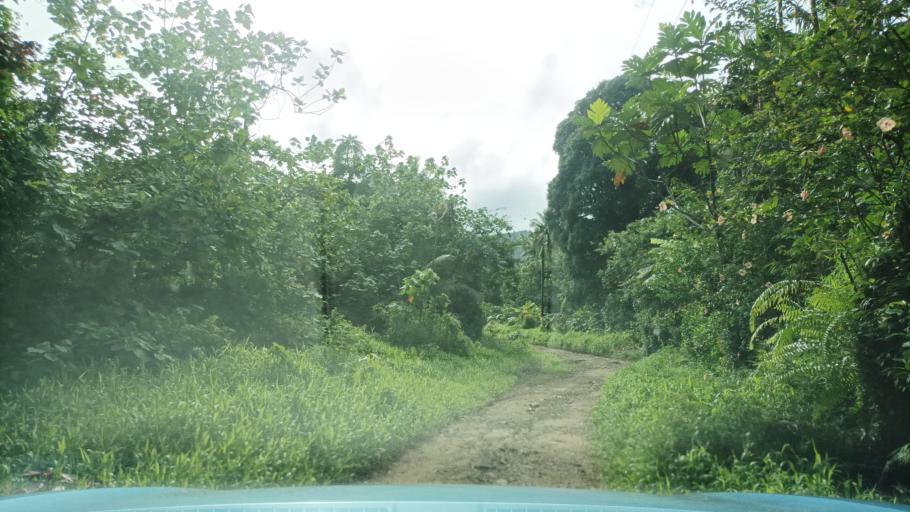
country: FM
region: Pohnpei
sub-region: Kolonia Municipality
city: Kolonia
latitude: 6.9304
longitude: 158.2394
